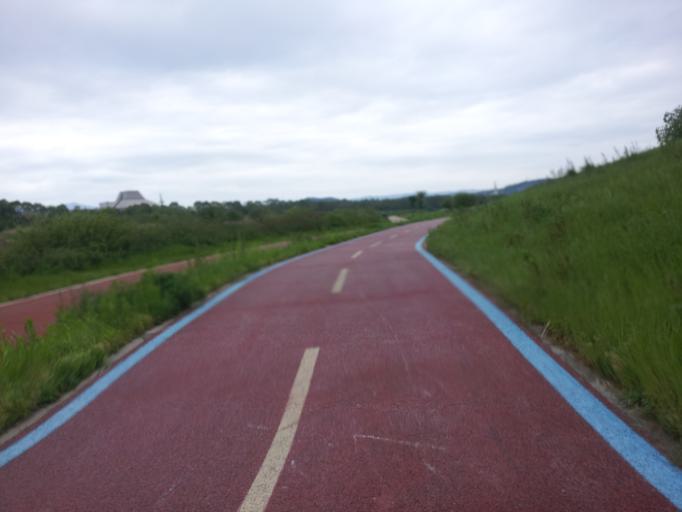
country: KR
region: Daejeon
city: Daejeon
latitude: 36.3635
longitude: 127.3985
